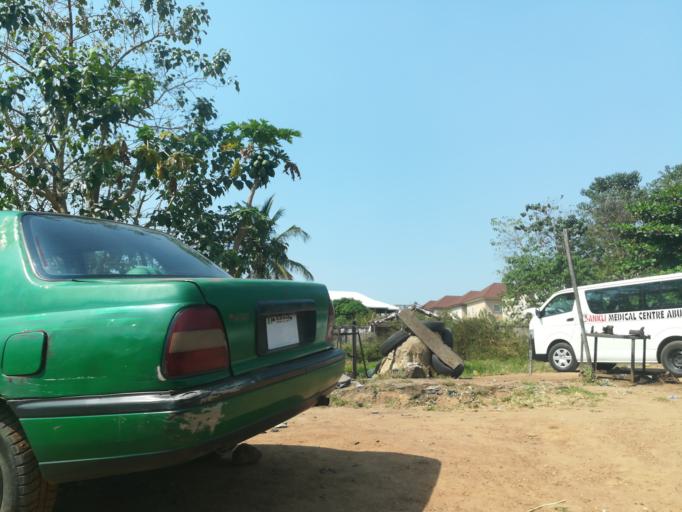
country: NG
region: Abuja Federal Capital Territory
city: Abuja
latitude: 9.0601
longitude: 7.4268
